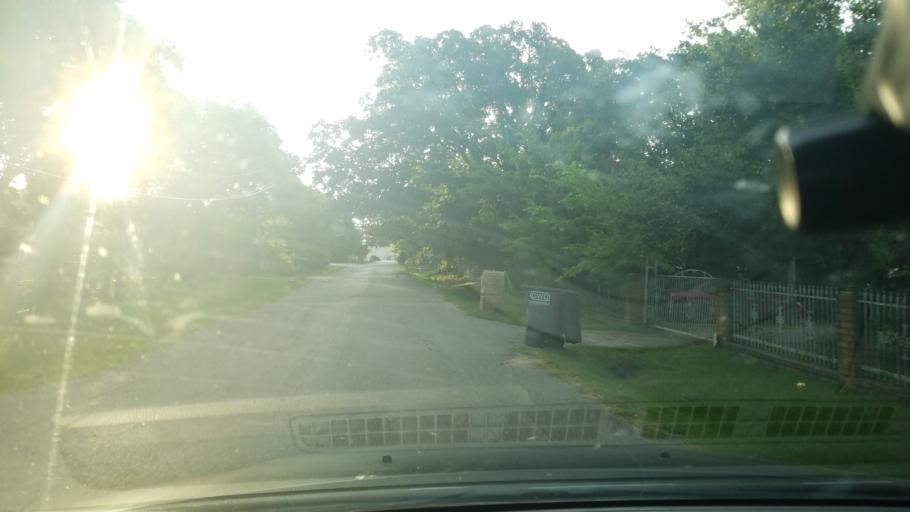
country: US
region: Texas
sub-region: Dallas County
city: Balch Springs
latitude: 32.7459
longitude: -96.6358
